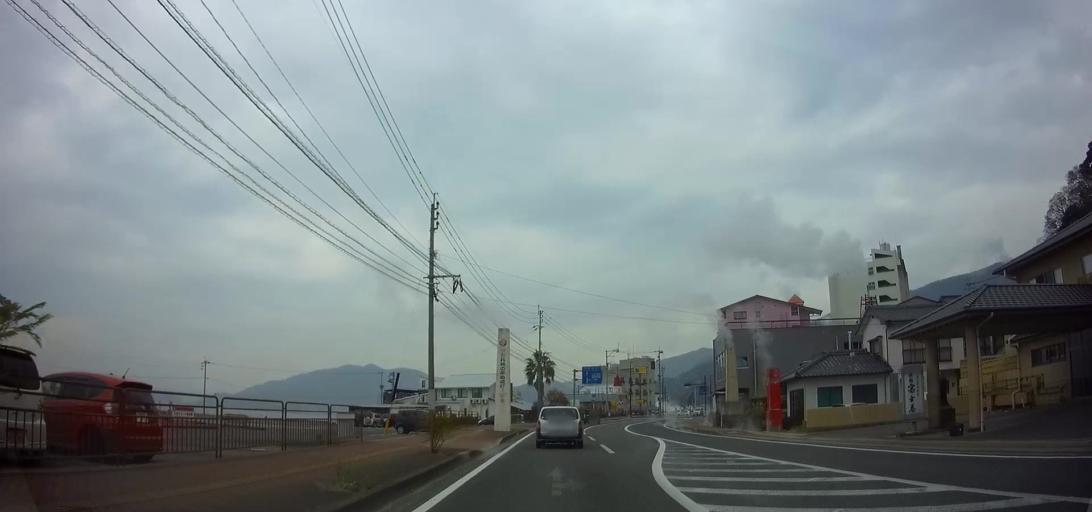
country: JP
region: Nagasaki
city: Shimabara
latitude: 32.7245
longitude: 130.2040
